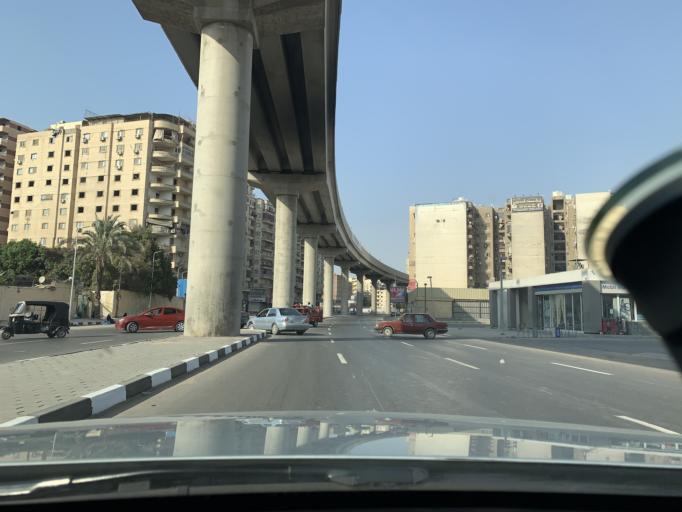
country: EG
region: Muhafazat al Qalyubiyah
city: Al Khankah
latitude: 30.1384
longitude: 31.3897
